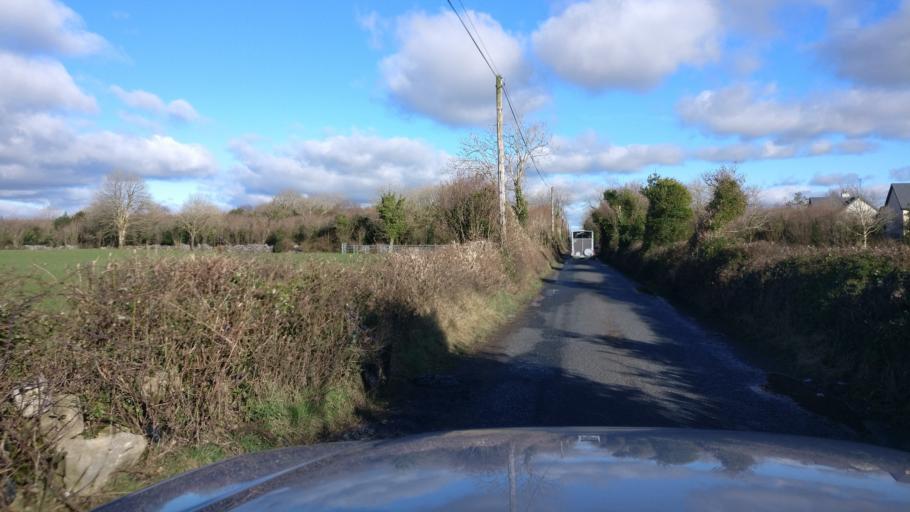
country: IE
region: Connaught
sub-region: County Galway
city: Oranmore
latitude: 53.2324
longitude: -8.8391
